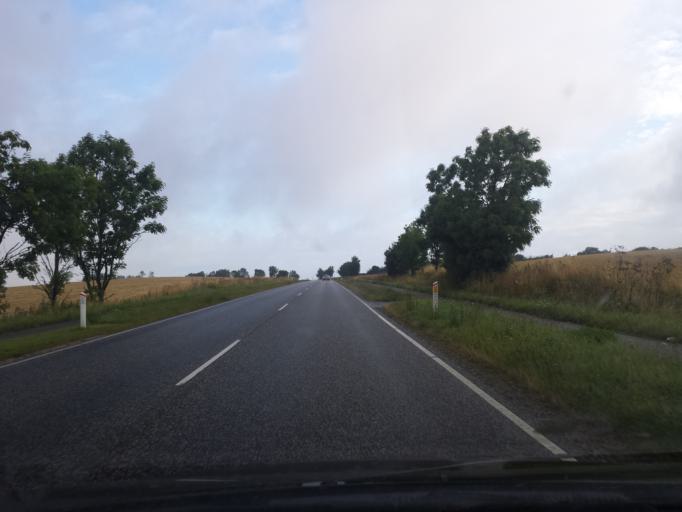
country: DK
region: South Denmark
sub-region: Sonderborg Kommune
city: Guderup
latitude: 55.0132
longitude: 9.8460
